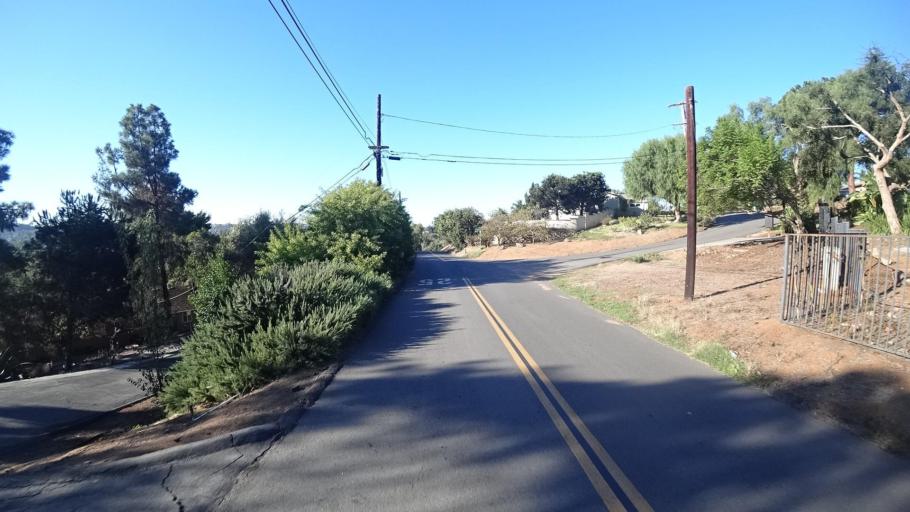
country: US
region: California
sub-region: San Diego County
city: Bonita
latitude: 32.6781
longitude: -117.0205
